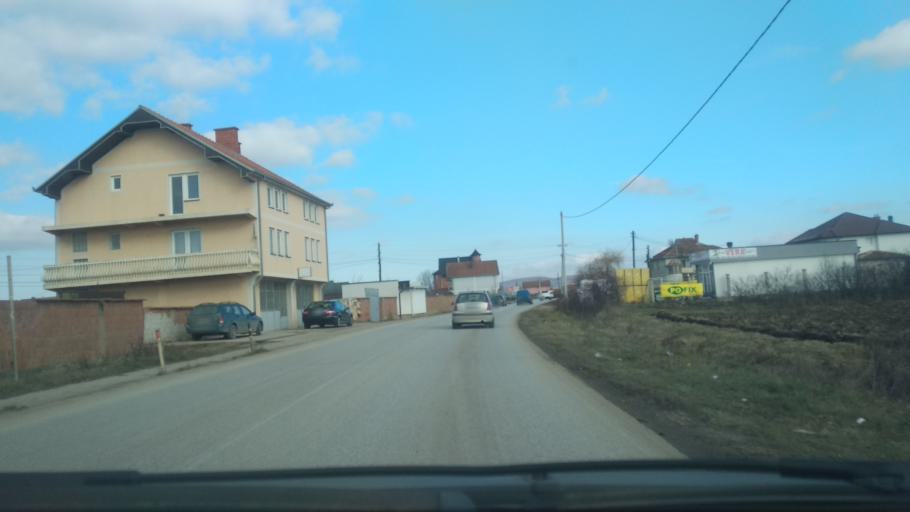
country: XK
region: Pristina
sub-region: Komuna e Obiliqit
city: Obiliq
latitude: 42.7324
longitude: 21.1053
